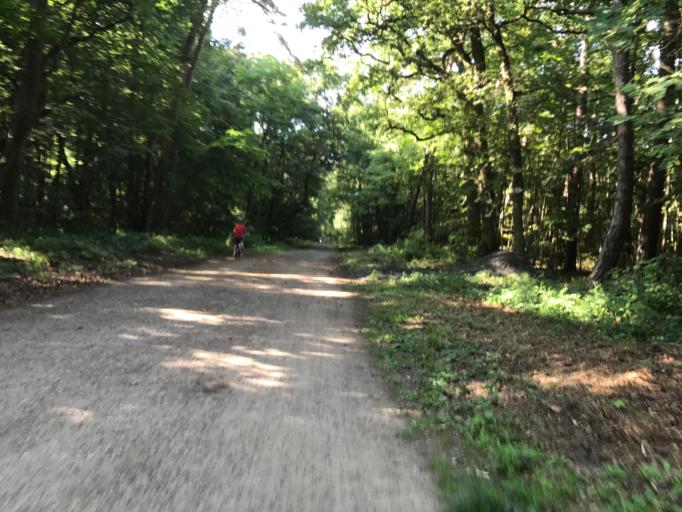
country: DE
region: Rheinland-Pfalz
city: Budenheim
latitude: 50.0116
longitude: 8.1903
